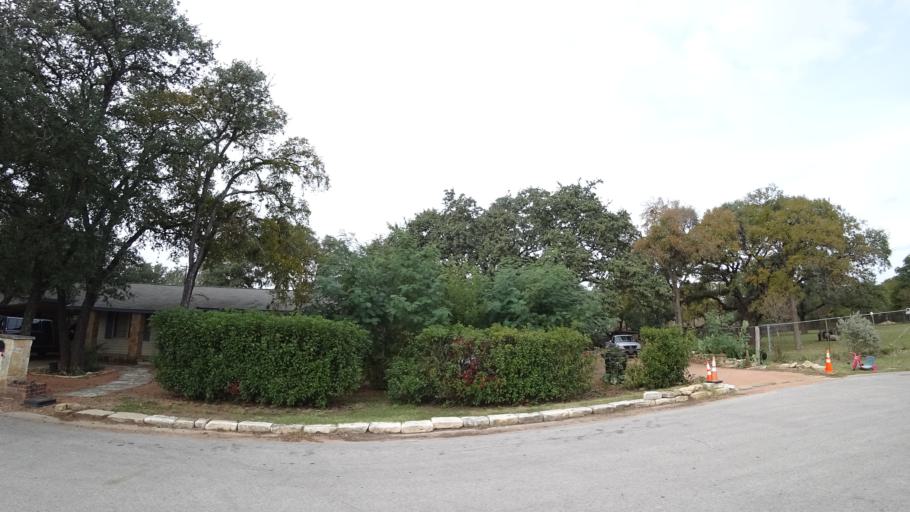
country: US
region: Texas
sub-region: Williamson County
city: Round Rock
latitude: 30.5140
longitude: -97.6623
